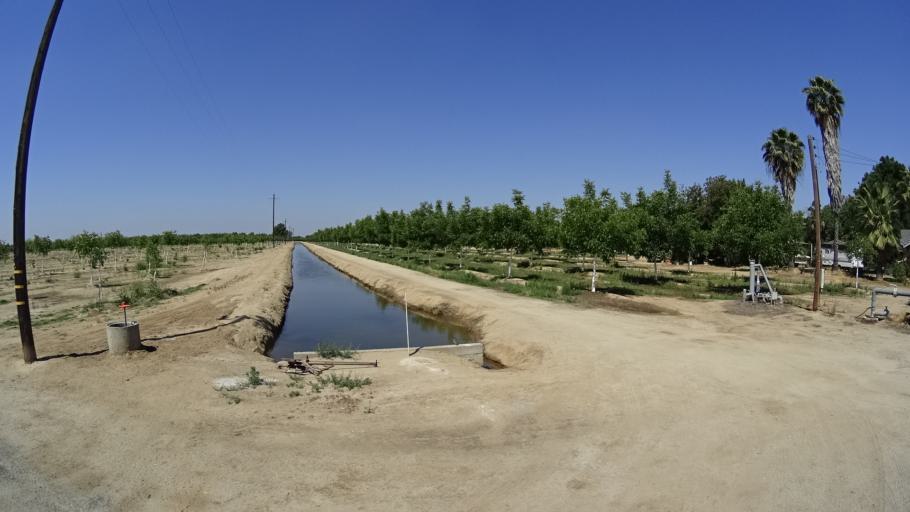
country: US
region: California
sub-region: Fresno County
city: Kingsburg
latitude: 36.4645
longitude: -119.5734
